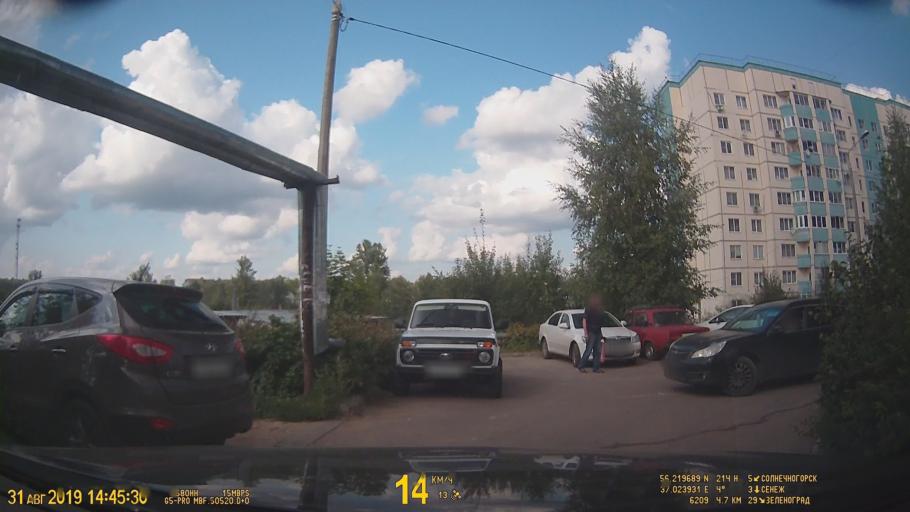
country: RU
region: Moskovskaya
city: Solnechnogorsk
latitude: 56.2197
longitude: 37.0239
